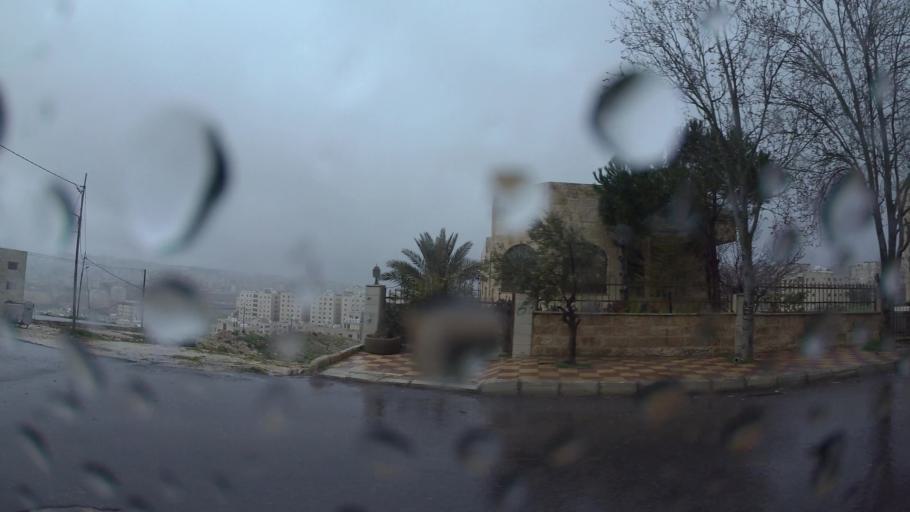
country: JO
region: Amman
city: Al Jubayhah
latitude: 32.0454
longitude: 35.8933
